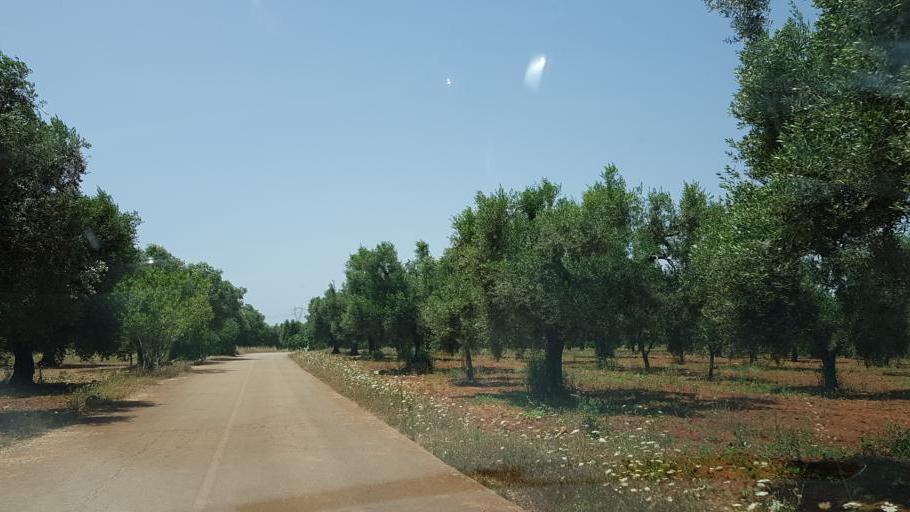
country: IT
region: Apulia
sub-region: Provincia di Lecce
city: Porto Cesareo
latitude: 40.3237
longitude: 17.8814
